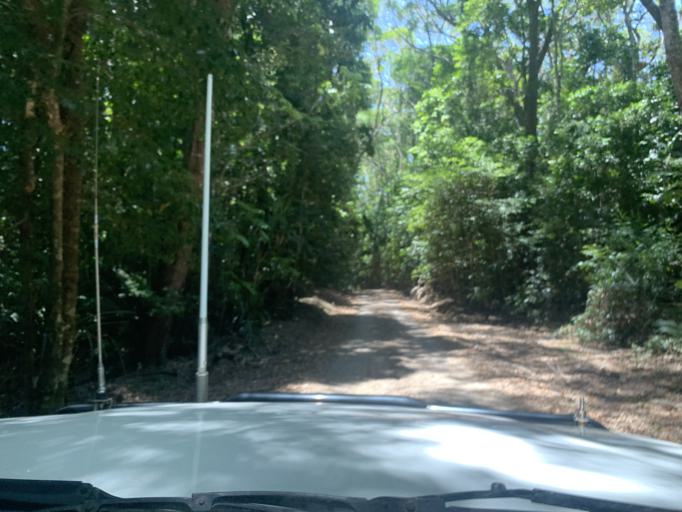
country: AU
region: Queensland
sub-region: Cairns
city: Redlynch
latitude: -16.9494
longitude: 145.6347
